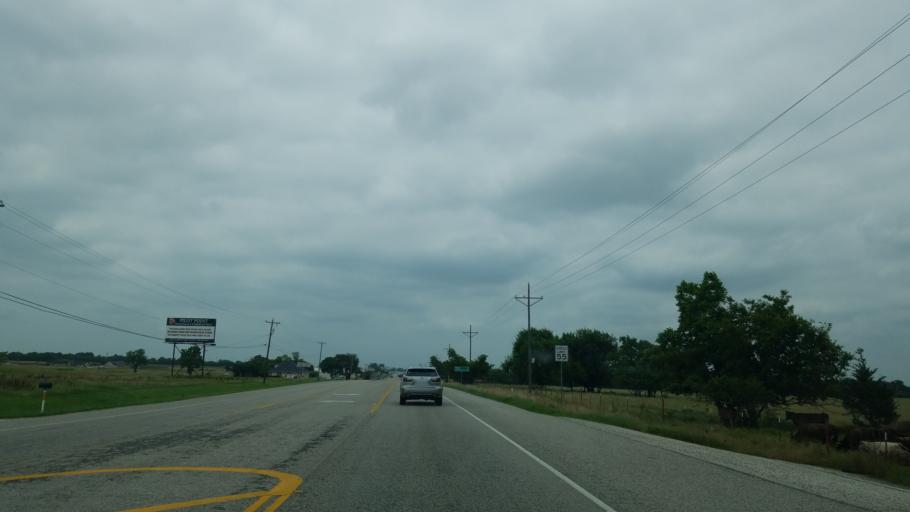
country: US
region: Texas
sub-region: Denton County
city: Pilot Point
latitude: 33.3961
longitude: -96.9456
